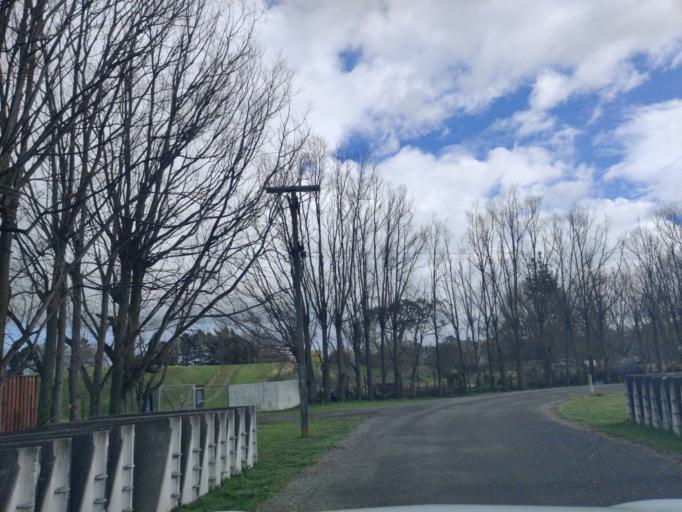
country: NZ
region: Manawatu-Wanganui
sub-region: Palmerston North City
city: Palmerston North
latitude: -40.2348
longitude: 175.5576
